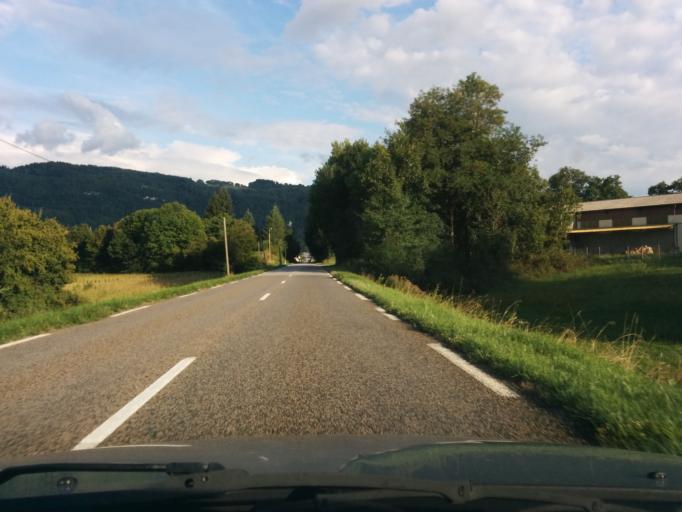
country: FR
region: Rhone-Alpes
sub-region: Departement de la Savoie
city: Saint-Beron
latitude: 45.5098
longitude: 5.7128
